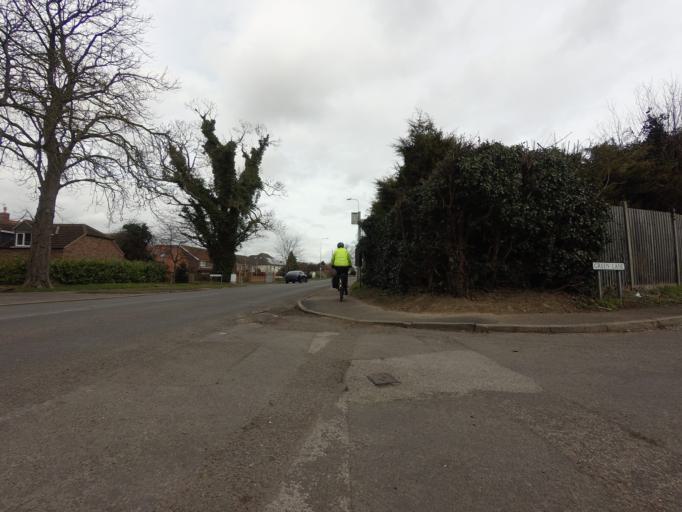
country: GB
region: England
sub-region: Lincolnshire
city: Grantham
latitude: 52.9260
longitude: -0.6278
